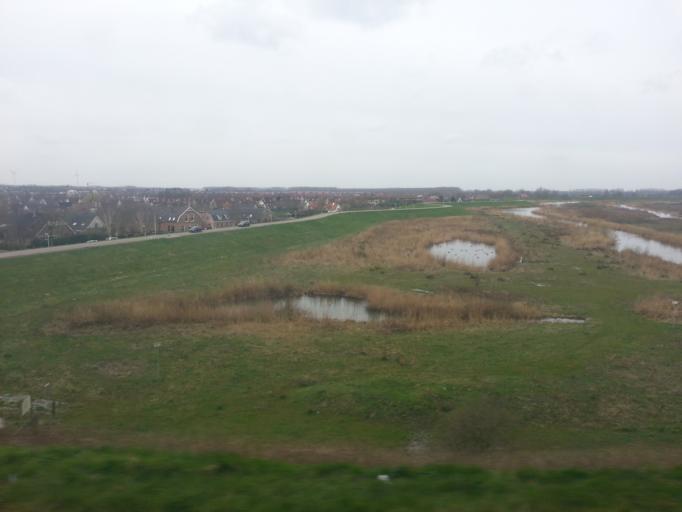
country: NL
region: Gelderland
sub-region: Gemeente Culemborg
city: Culemborg
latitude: 51.9575
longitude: 5.2165
